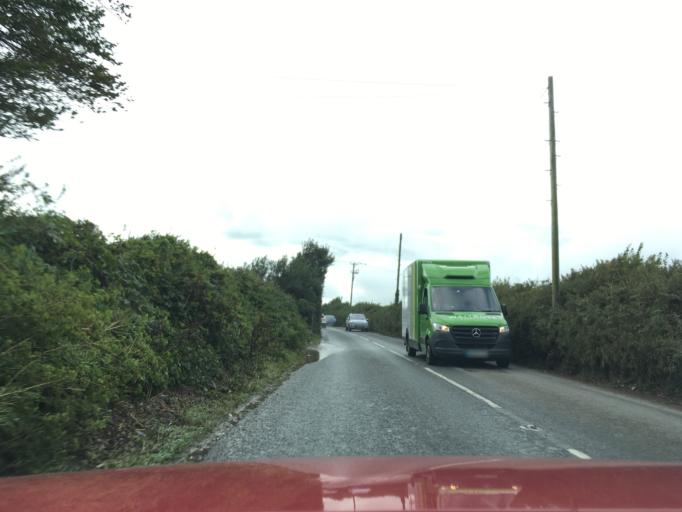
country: GB
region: England
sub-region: Devon
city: Kingsbridge
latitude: 50.2983
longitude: -3.8214
